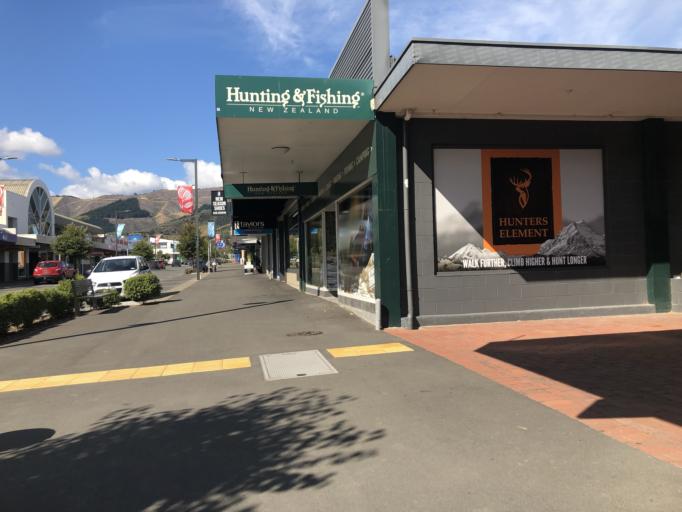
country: NZ
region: Tasman
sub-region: Tasman District
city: Richmond
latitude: -41.3398
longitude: 173.1853
